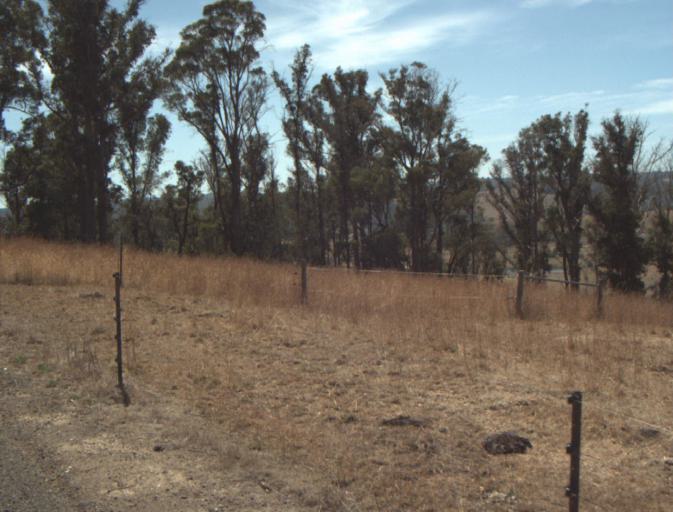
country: AU
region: Tasmania
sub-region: Launceston
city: Mayfield
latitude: -41.2480
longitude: 147.1347
